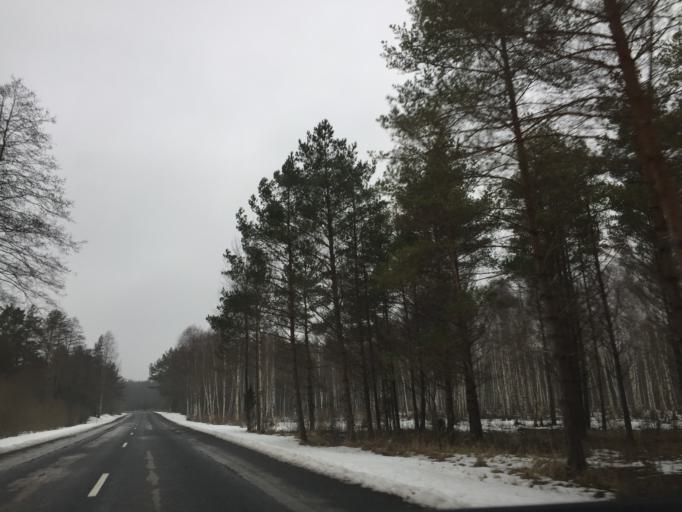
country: EE
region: Saare
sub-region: Orissaare vald
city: Orissaare
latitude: 58.3882
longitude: 22.8617
